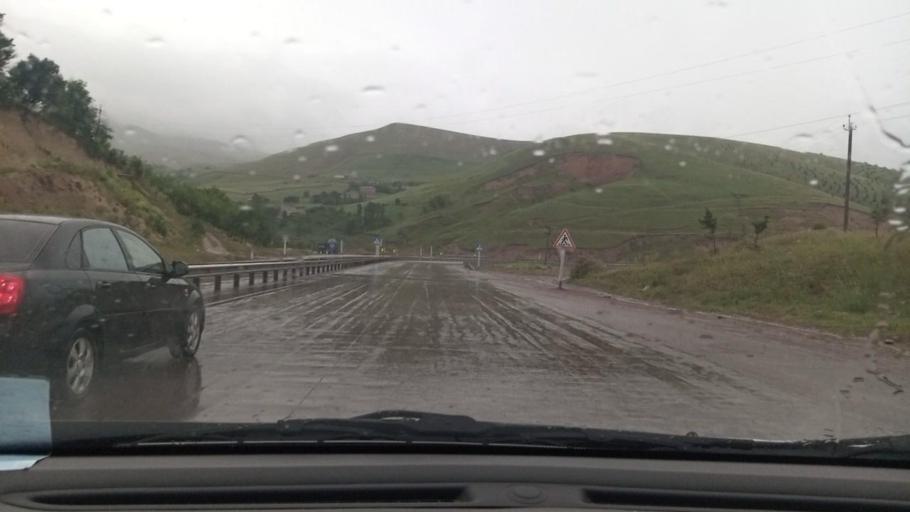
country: UZ
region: Toshkent
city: Angren
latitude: 41.0663
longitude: 70.2196
